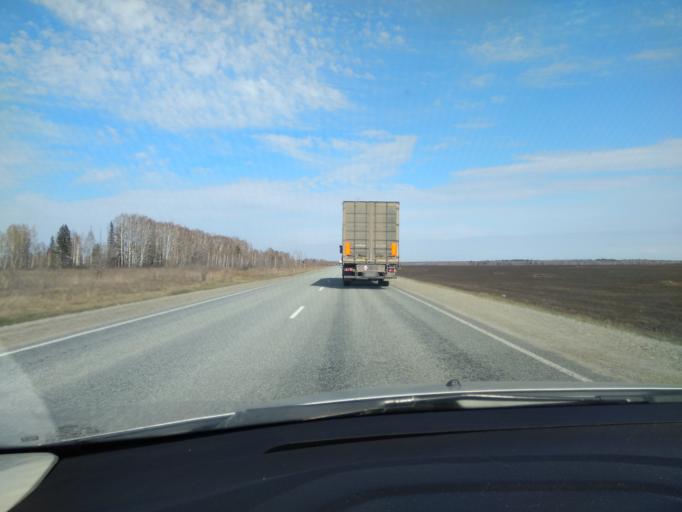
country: RU
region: Sverdlovsk
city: Tugulym
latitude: 57.0716
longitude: 64.6916
